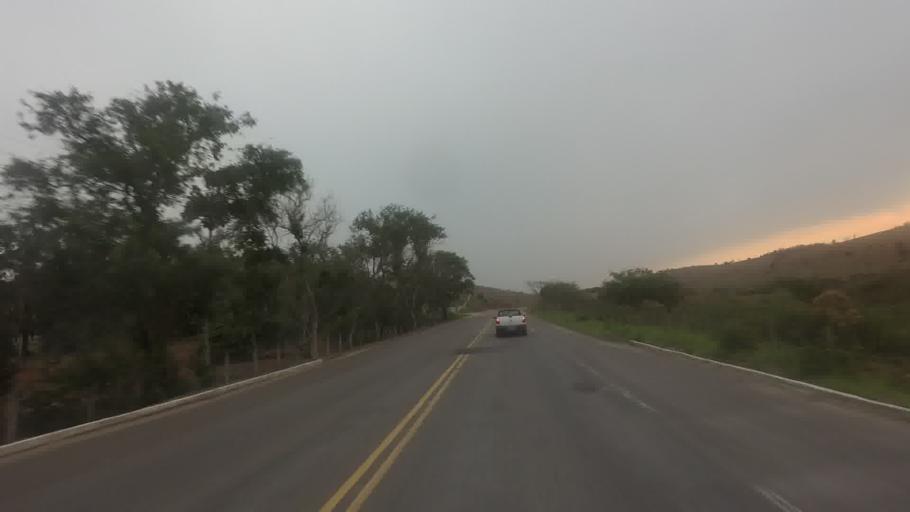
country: BR
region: Minas Gerais
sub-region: Recreio
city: Recreio
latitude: -21.6620
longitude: -42.3773
